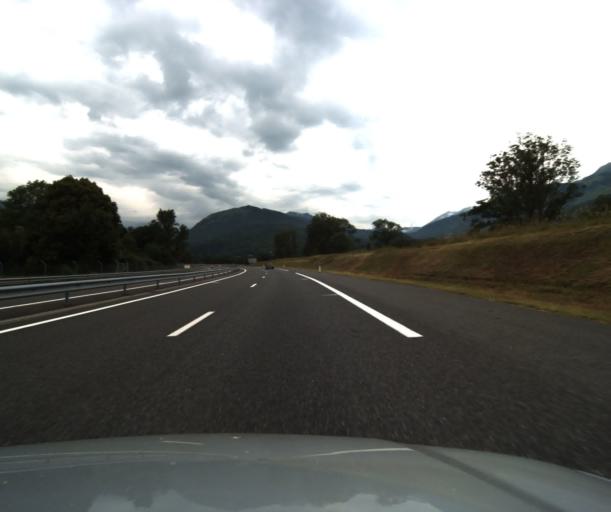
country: FR
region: Midi-Pyrenees
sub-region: Departement des Hautes-Pyrenees
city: Argeles-Gazost
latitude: 43.0277
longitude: -0.0799
